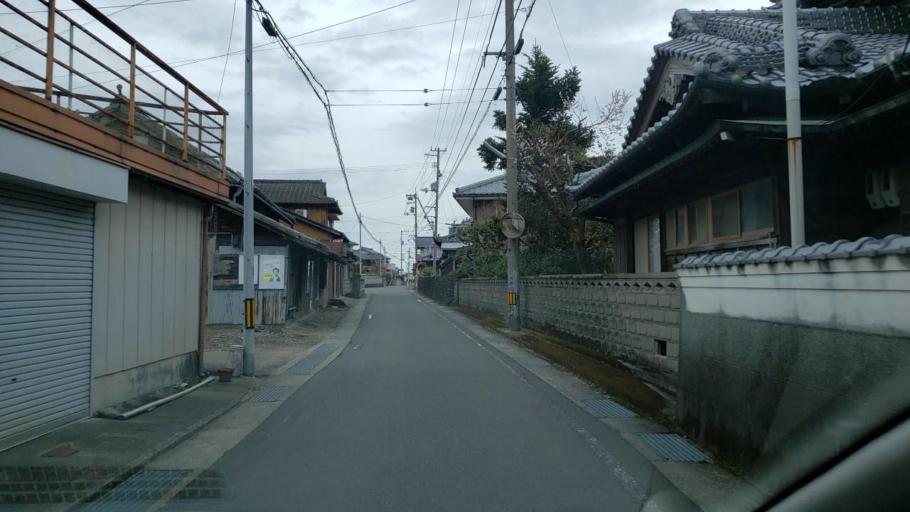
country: JP
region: Tokushima
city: Kamojimacho-jogejima
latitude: 34.0898
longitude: 134.2961
